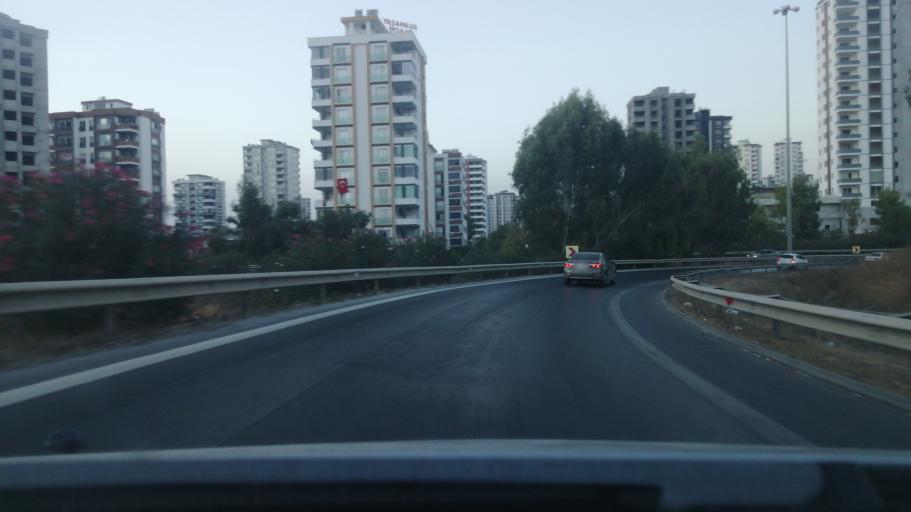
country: TR
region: Adana
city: Seyhan
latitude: 37.0335
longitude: 35.2506
